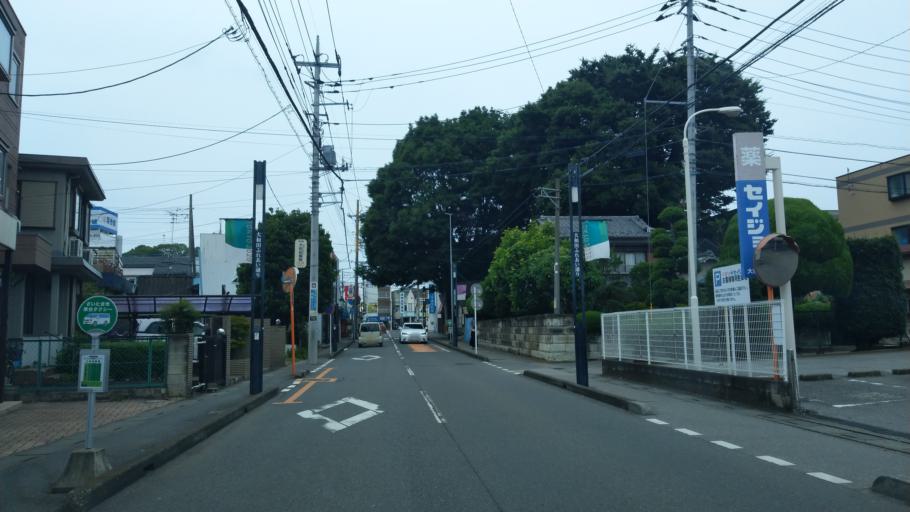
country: JP
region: Saitama
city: Saitama
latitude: 35.9282
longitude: 139.6504
